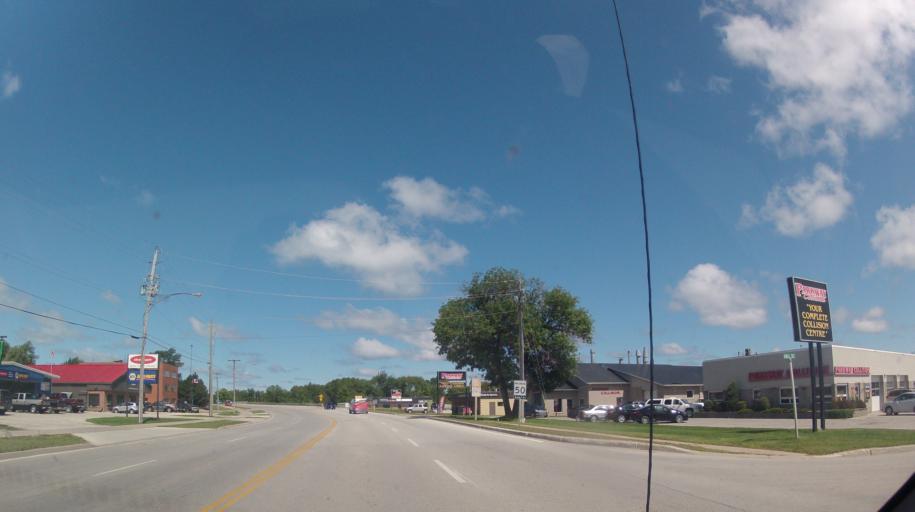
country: CA
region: Ontario
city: Collingwood
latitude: 44.5010
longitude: -80.1965
